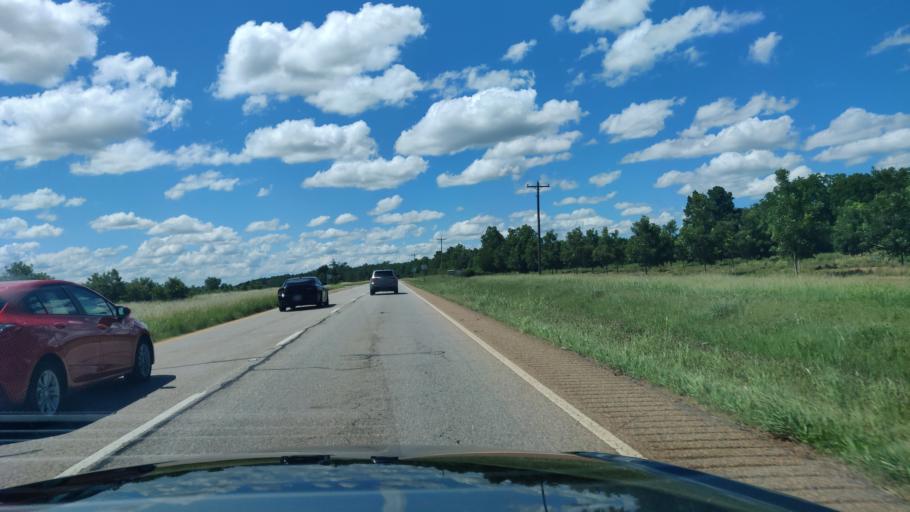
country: US
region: Georgia
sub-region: Webster County
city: Preston
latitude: 31.9417
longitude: -84.5699
